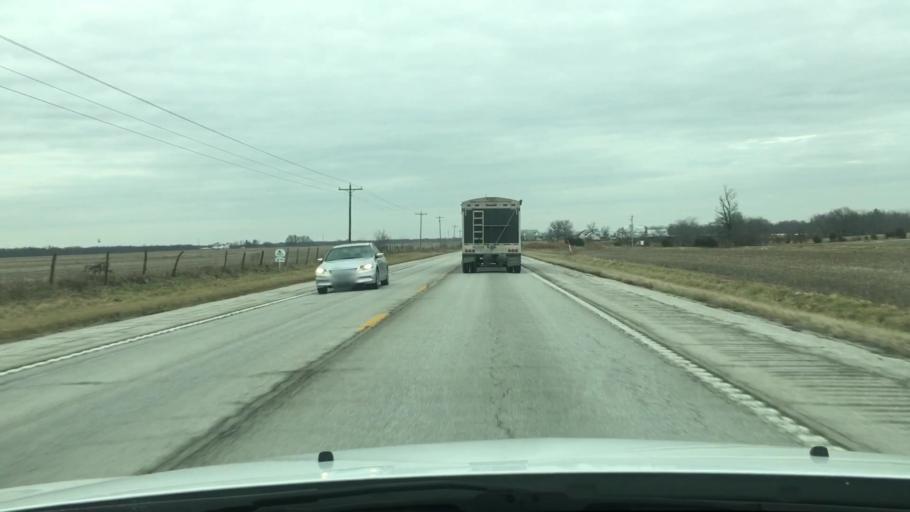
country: US
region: Missouri
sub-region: Montgomery County
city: Wellsville
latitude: 39.1714
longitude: -91.6477
